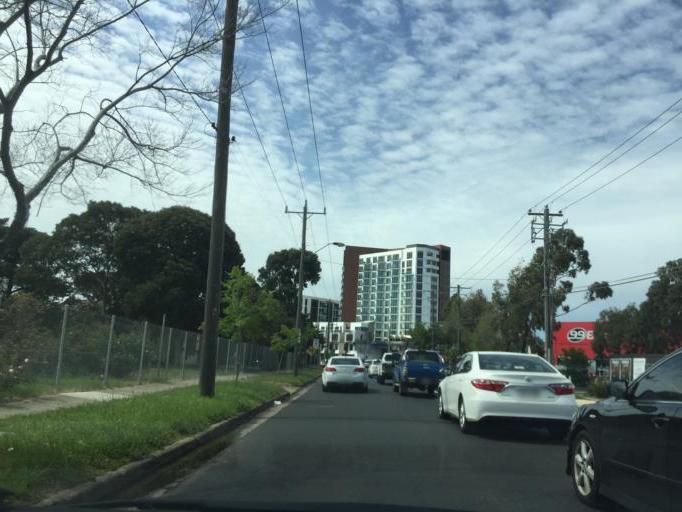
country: AU
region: Victoria
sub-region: Maribyrnong
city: Maidstone
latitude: -37.7761
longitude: 144.8794
